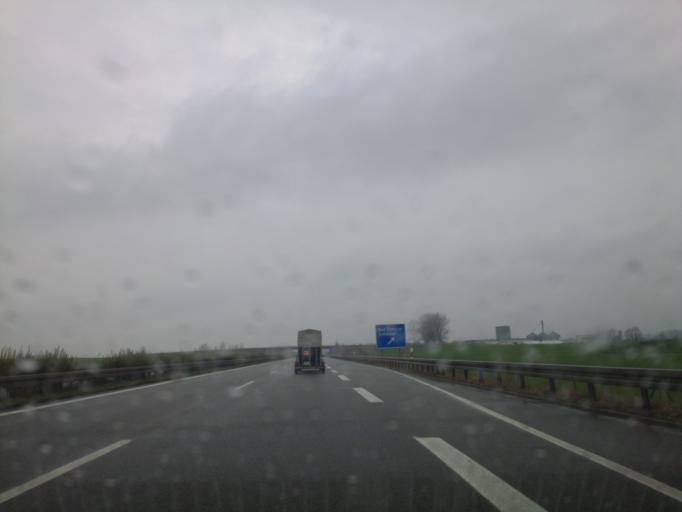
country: DE
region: Mecklenburg-Vorpommern
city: Ziesendorf
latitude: 54.0094
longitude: 12.0300
